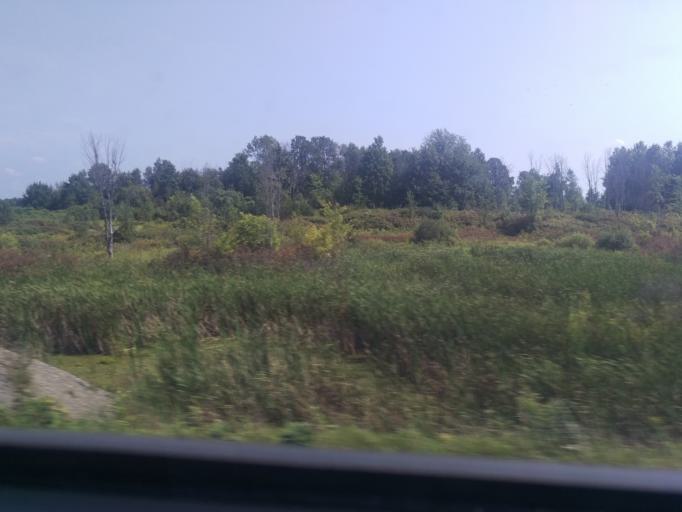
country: US
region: New York
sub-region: Jefferson County
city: Alexandria Bay
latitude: 44.4533
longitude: -75.9294
